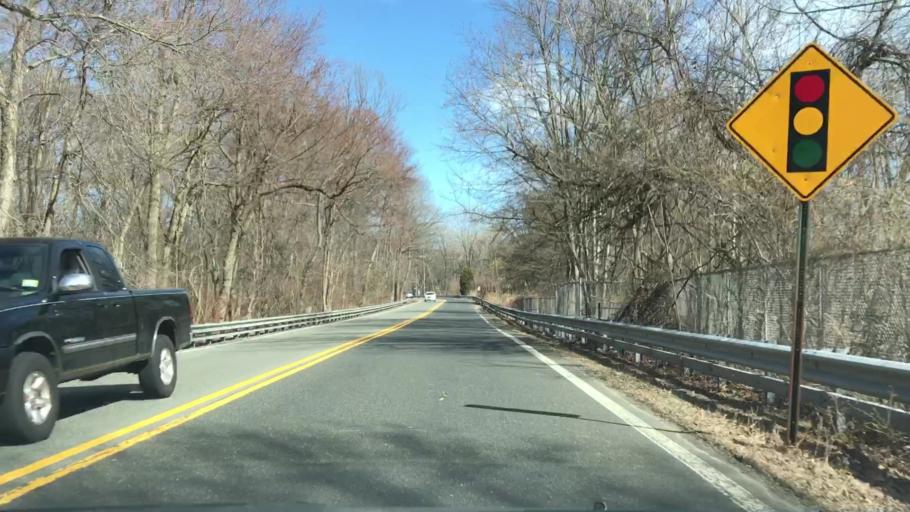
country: US
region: New Jersey
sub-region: Bergen County
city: Closter
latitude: 40.9855
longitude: -73.9639
